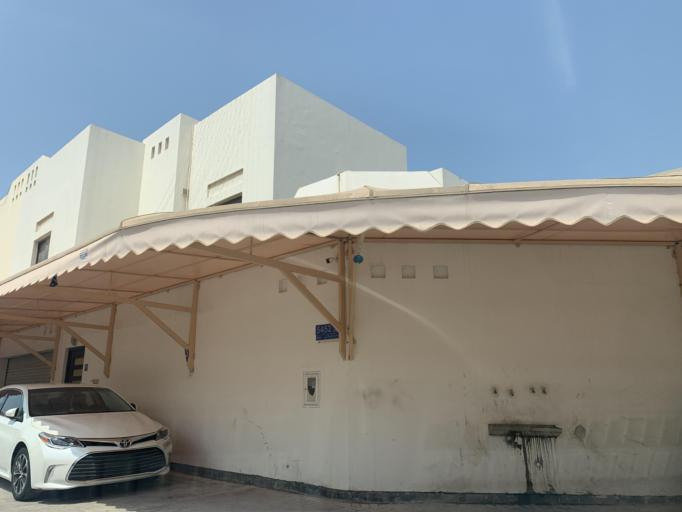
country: BH
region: Muharraq
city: Al Hadd
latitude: 26.2677
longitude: 50.6598
